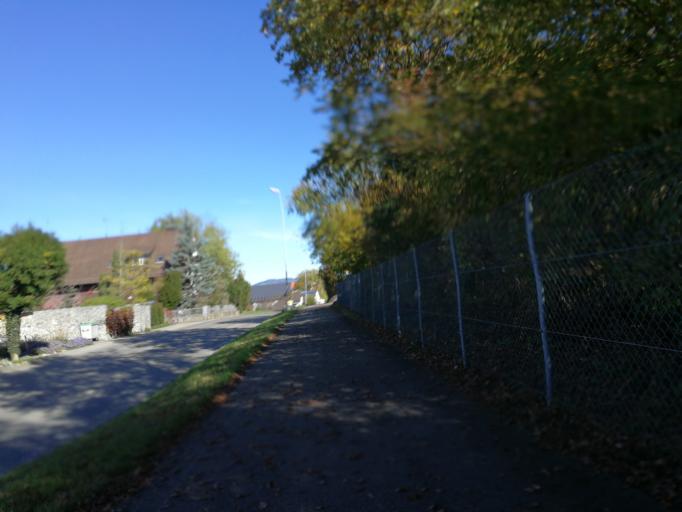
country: CH
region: Zurich
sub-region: Bezirk Meilen
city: Oetwil am See
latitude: 47.2703
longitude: 8.7398
